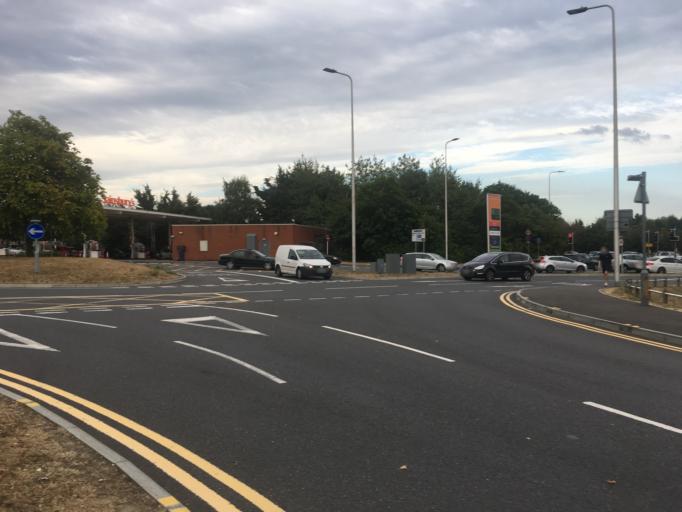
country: GB
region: England
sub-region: West Berkshire
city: Calcot
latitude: 51.4415
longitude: -1.0614
